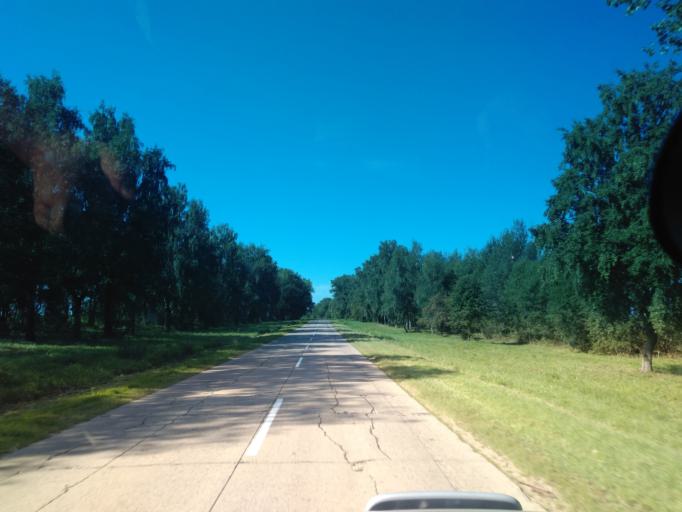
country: BY
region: Minsk
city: Stan'kava
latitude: 53.6457
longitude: 27.2984
